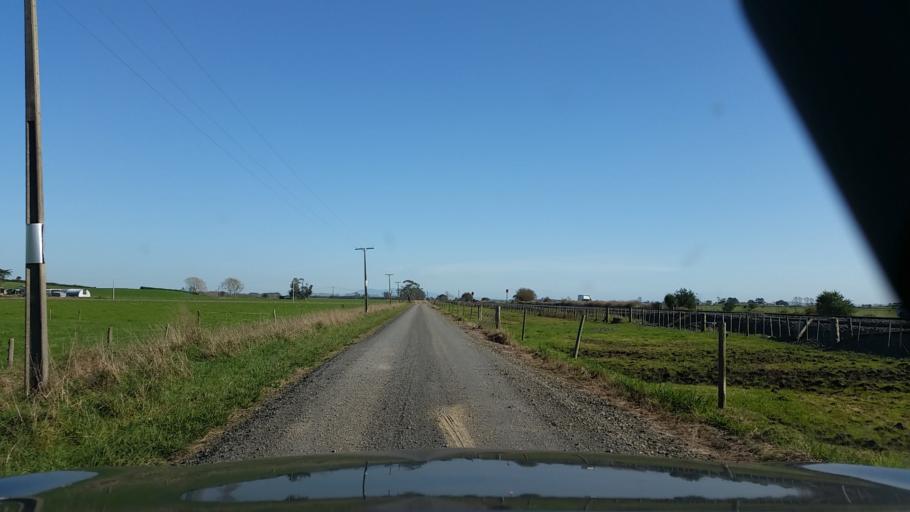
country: NZ
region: Waikato
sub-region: Waipa District
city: Cambridge
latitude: -37.6795
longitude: 175.4589
